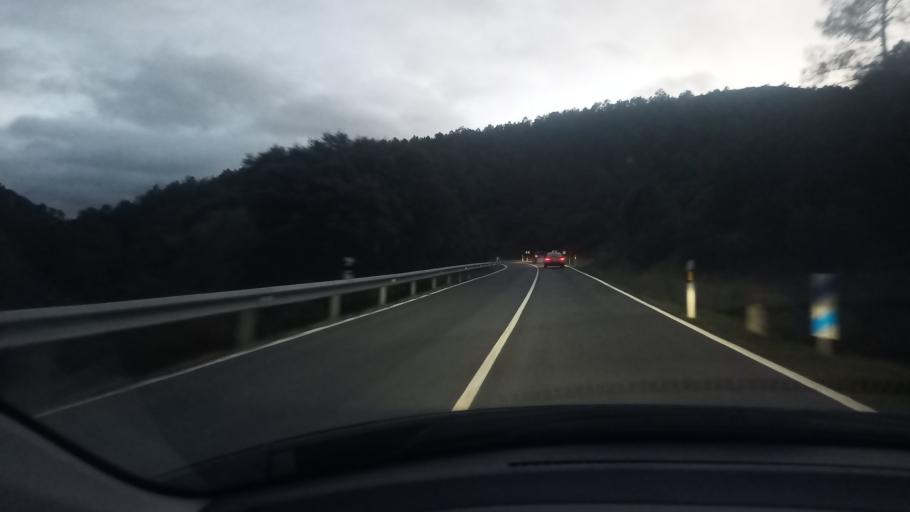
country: ES
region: Madrid
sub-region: Provincia de Madrid
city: Robledo de Chavela
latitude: 40.4583
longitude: -4.2637
